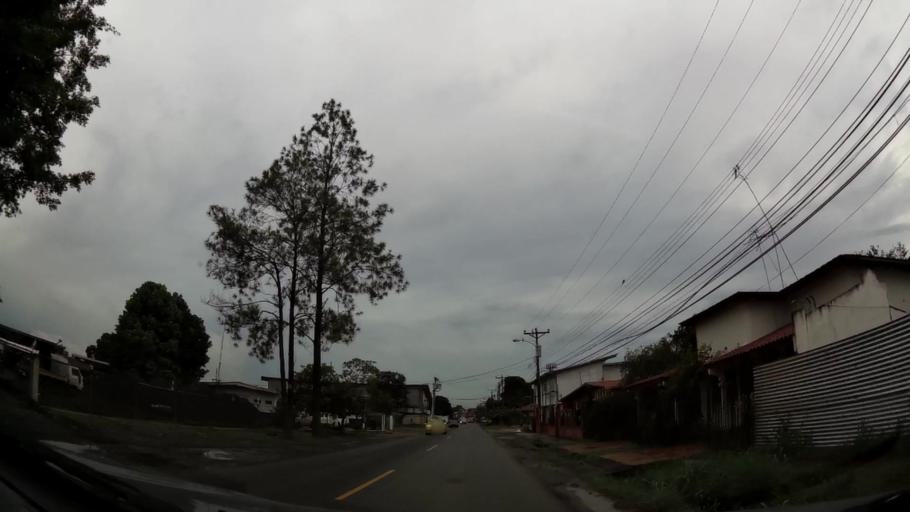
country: PA
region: Veraguas
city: Santiago de Veraguas
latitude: 8.1085
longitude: -80.9739
